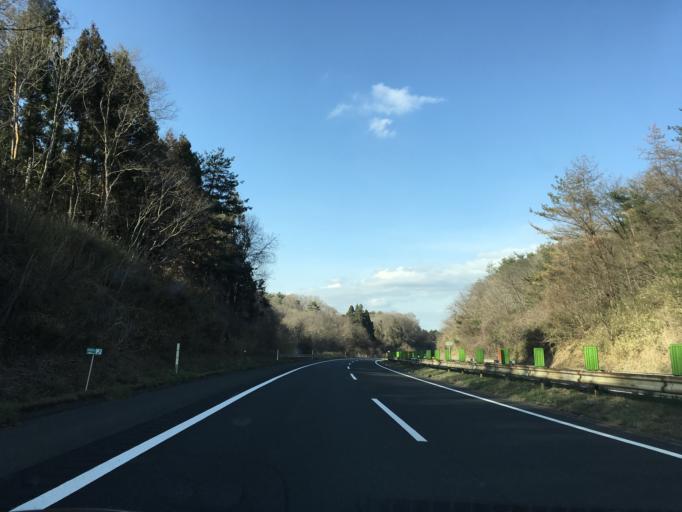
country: JP
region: Iwate
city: Ichinoseki
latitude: 38.9044
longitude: 141.0890
